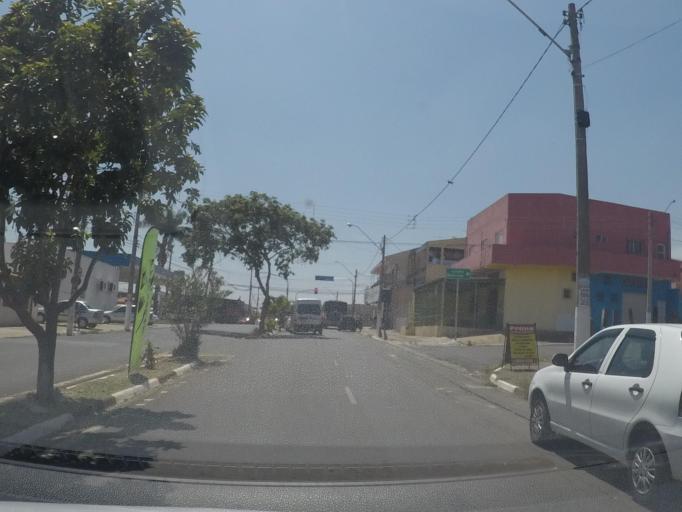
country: BR
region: Sao Paulo
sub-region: Hortolandia
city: Hortolandia
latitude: -22.8582
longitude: -47.2153
